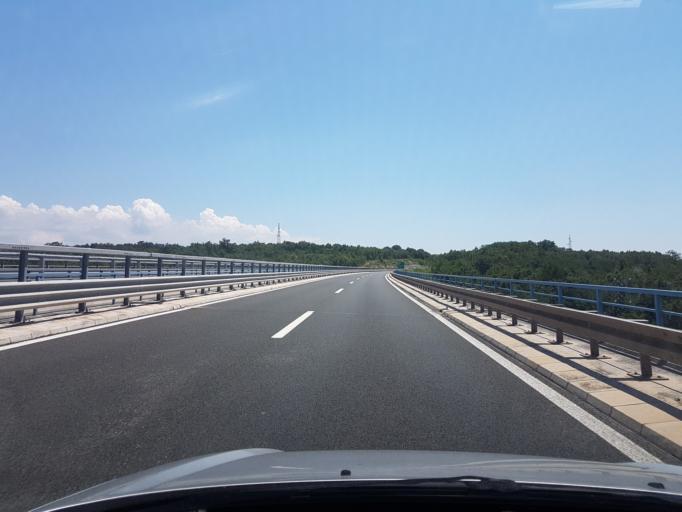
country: HR
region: Istarska
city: Buje
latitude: 45.3727
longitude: 13.6231
